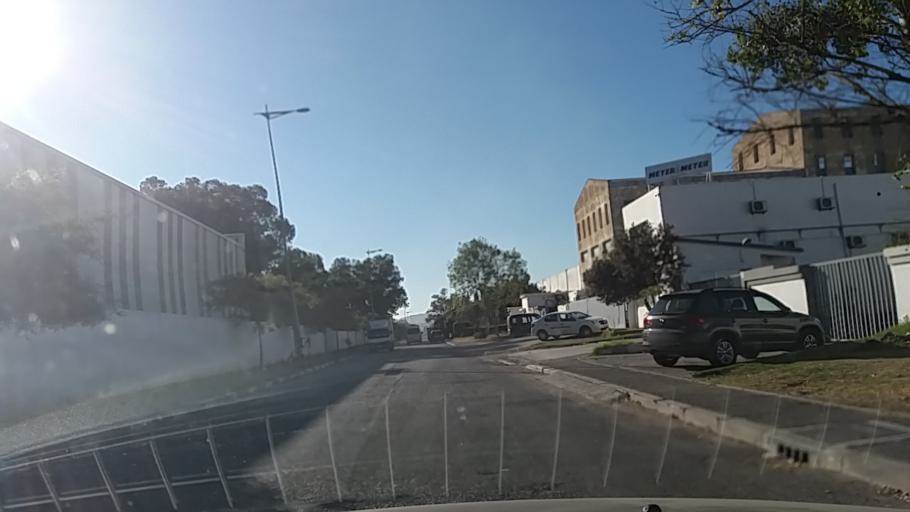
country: MA
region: Tanger-Tetouan
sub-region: Tanger-Assilah
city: Tangier
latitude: 35.7373
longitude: -5.7740
